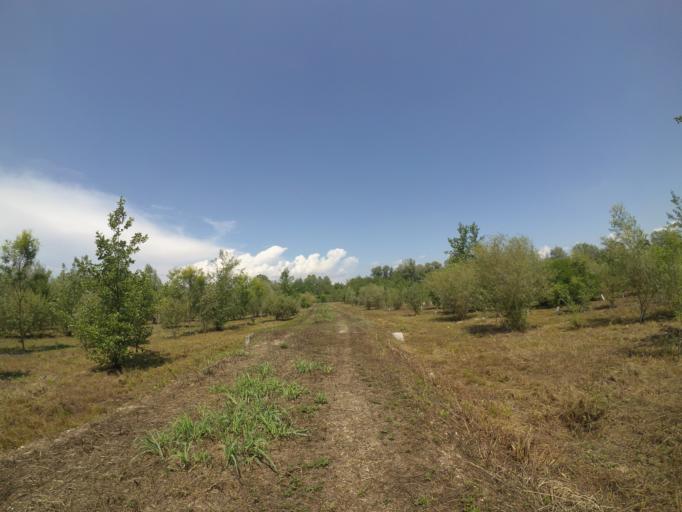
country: IT
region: Friuli Venezia Giulia
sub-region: Provincia di Udine
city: Rivignano
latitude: 45.8970
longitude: 13.0710
